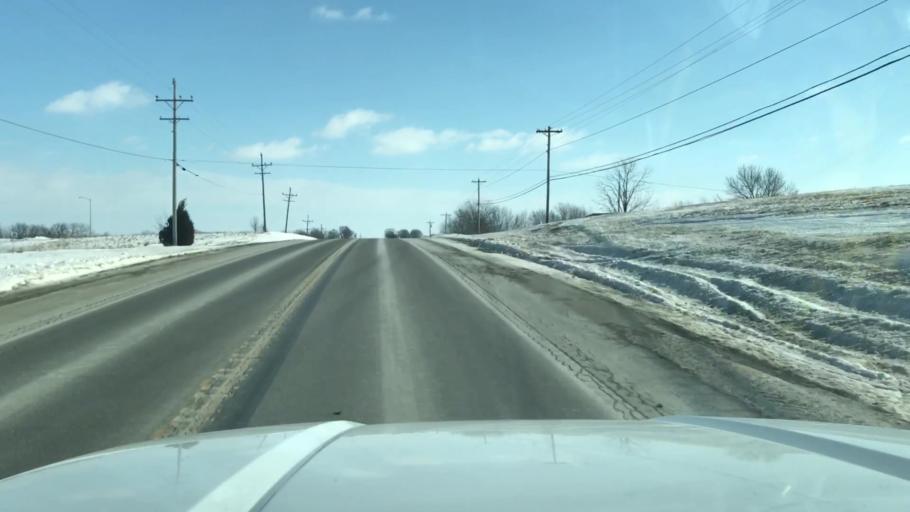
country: US
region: Missouri
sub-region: Nodaway County
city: Maryville
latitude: 40.3446
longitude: -94.8072
